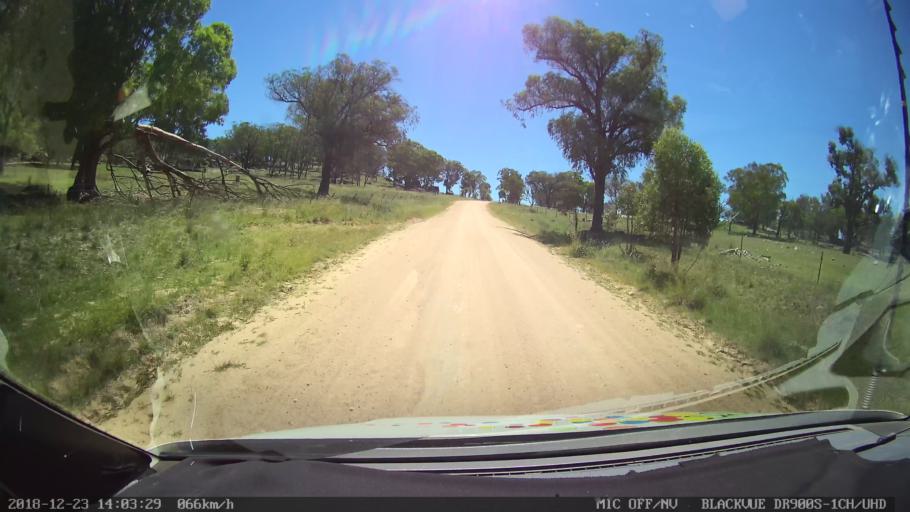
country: AU
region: New South Wales
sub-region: Tamworth Municipality
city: Manilla
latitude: -30.6234
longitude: 151.0998
